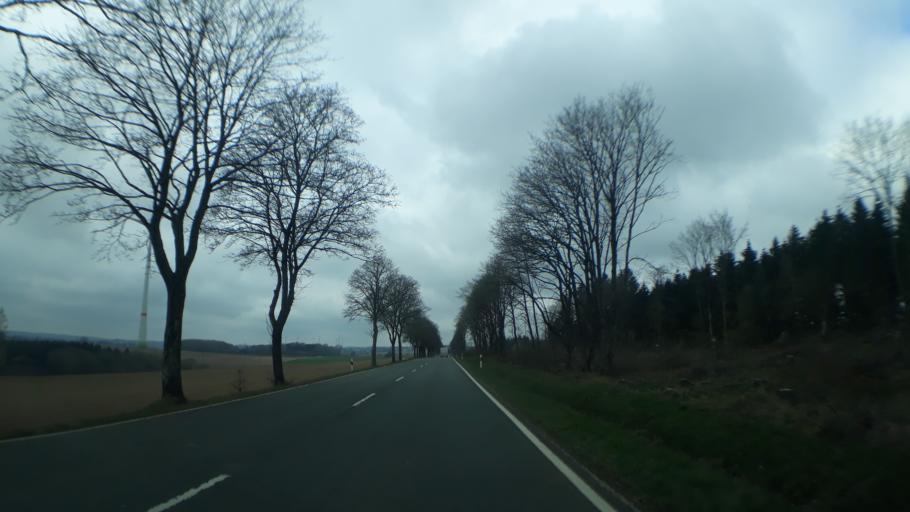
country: DE
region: North Rhine-Westphalia
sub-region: Regierungsbezirk Koln
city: Schleiden
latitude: 50.5545
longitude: 6.4432
